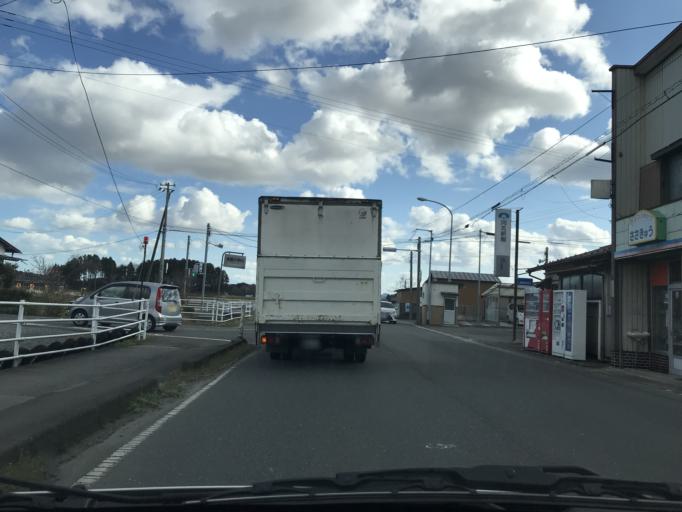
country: JP
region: Miyagi
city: Wakuya
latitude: 38.6609
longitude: 141.1932
